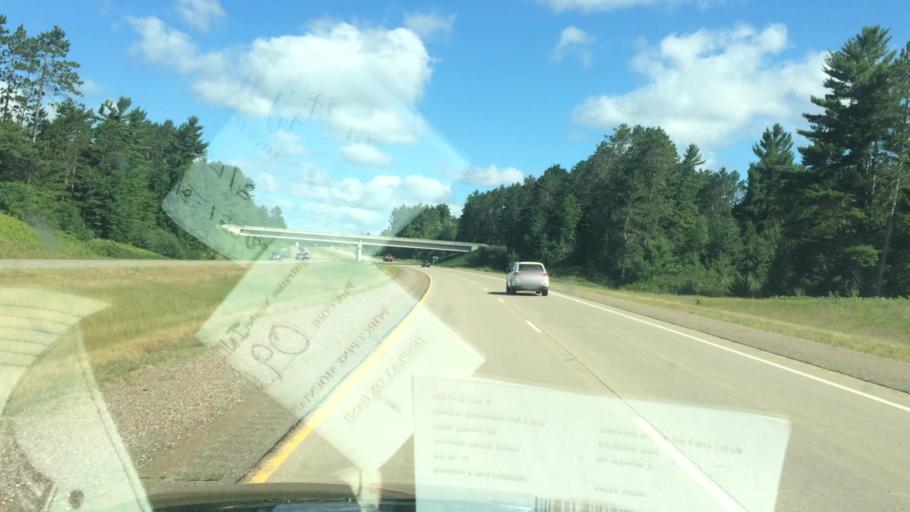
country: US
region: Wisconsin
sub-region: Lincoln County
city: Tomahawk
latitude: 45.4357
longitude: -89.6803
